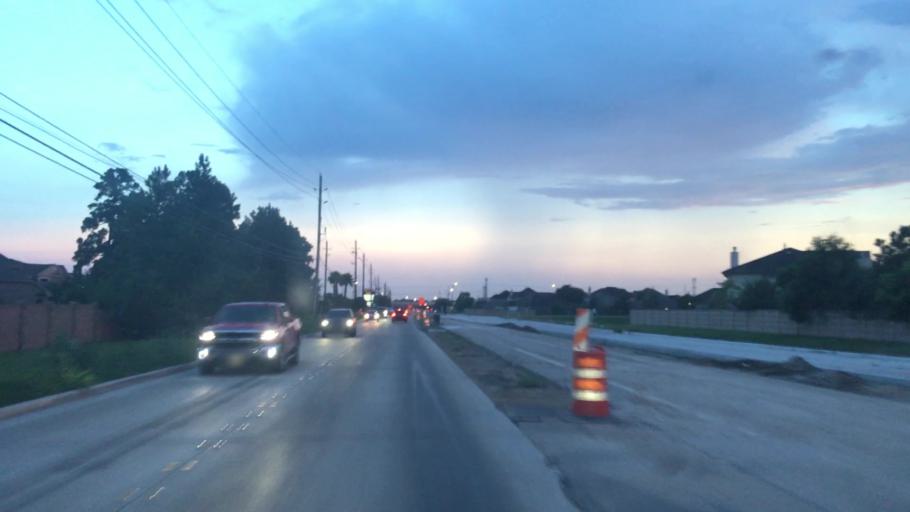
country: US
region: Texas
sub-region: Harris County
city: Humble
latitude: 29.9412
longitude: -95.2496
